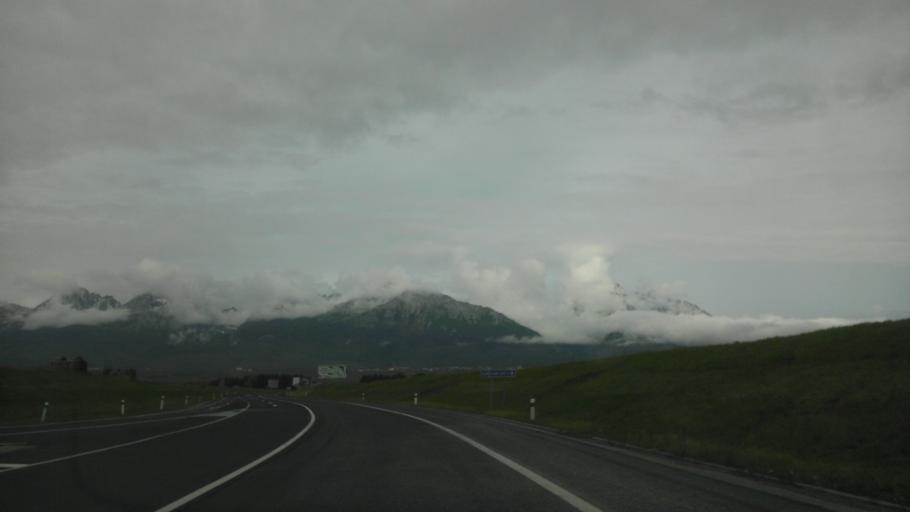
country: SK
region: Presovsky
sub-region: Okres Poprad
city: Poprad
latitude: 49.0743
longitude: 20.2751
